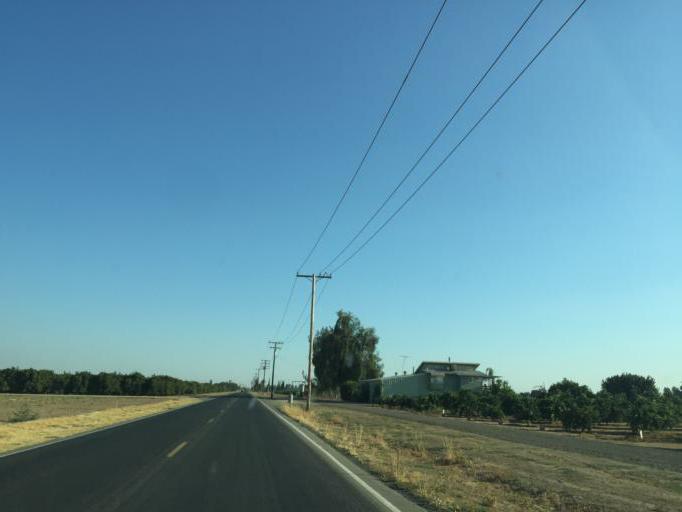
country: US
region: California
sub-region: Tulare County
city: Ivanhoe
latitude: 36.4080
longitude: -119.2782
